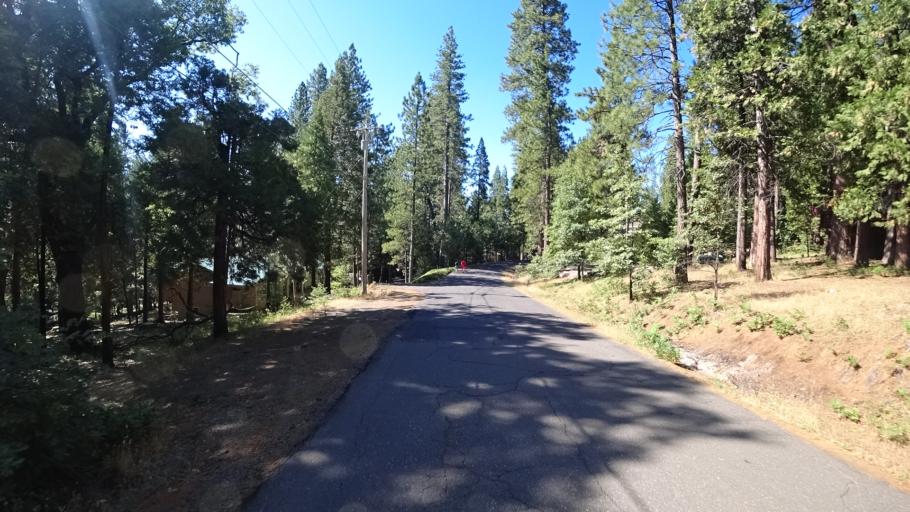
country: US
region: California
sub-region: Calaveras County
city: Arnold
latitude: 38.2445
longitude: -120.3642
